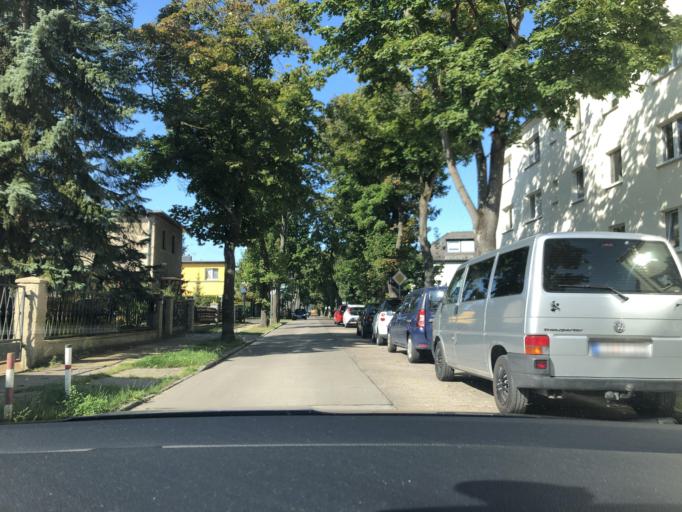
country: DE
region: Brandenburg
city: Erkner
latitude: 52.4155
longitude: 13.7415
